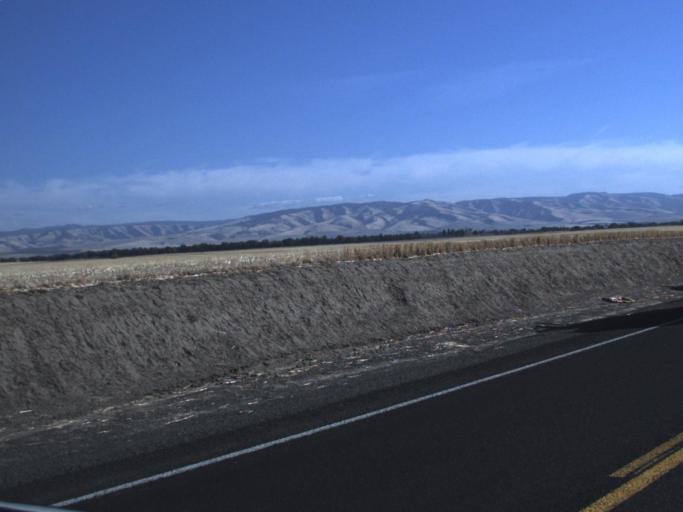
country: US
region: Washington
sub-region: Walla Walla County
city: Walla Walla
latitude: 46.0944
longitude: -118.3682
